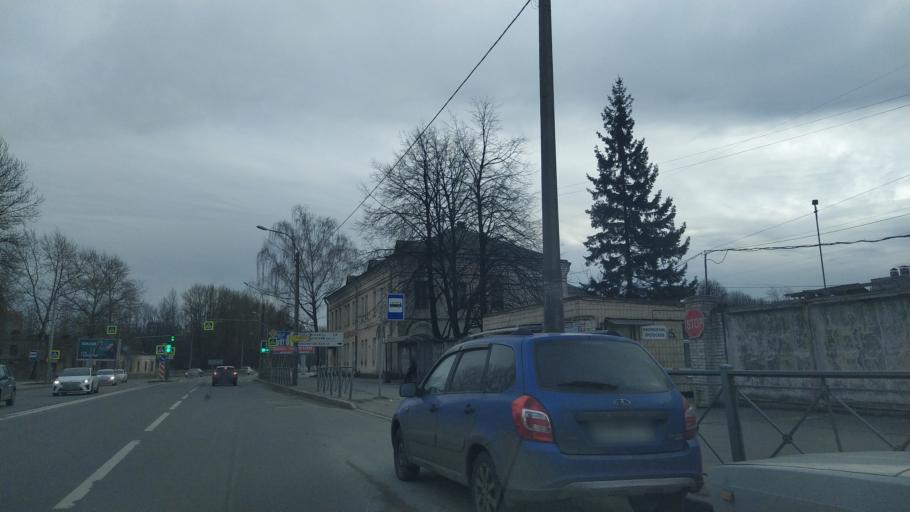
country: RU
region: St.-Petersburg
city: Kushelevka
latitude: 59.9845
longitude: 30.3612
